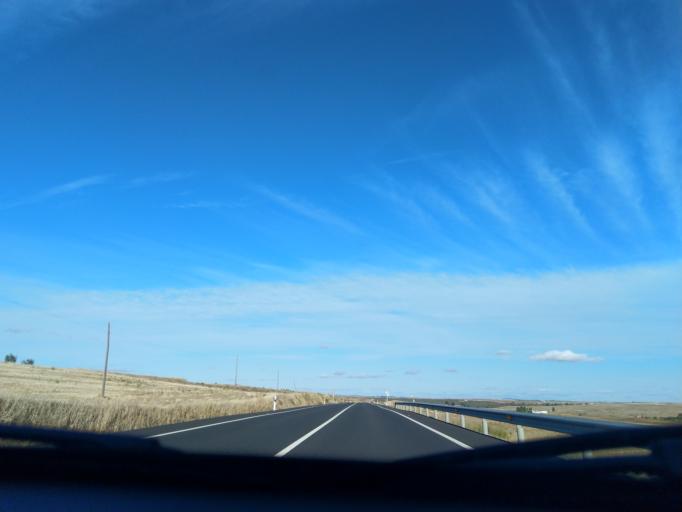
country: ES
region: Extremadura
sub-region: Provincia de Badajoz
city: Ahillones
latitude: 38.2653
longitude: -5.8501
